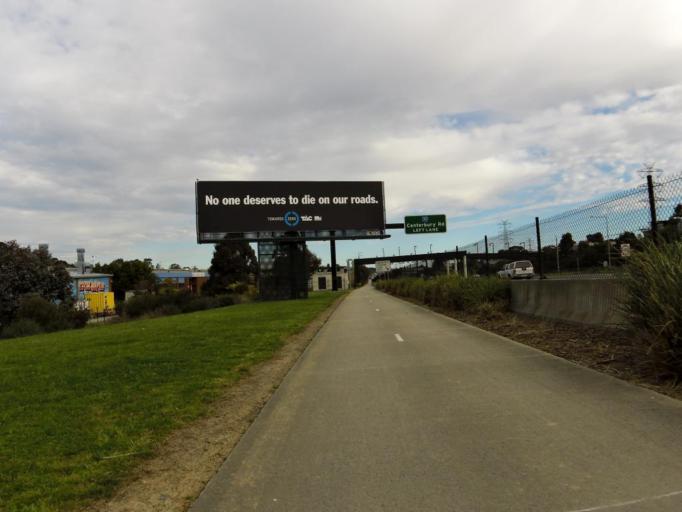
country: AU
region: Victoria
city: Mitcham
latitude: -37.8226
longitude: 145.2178
